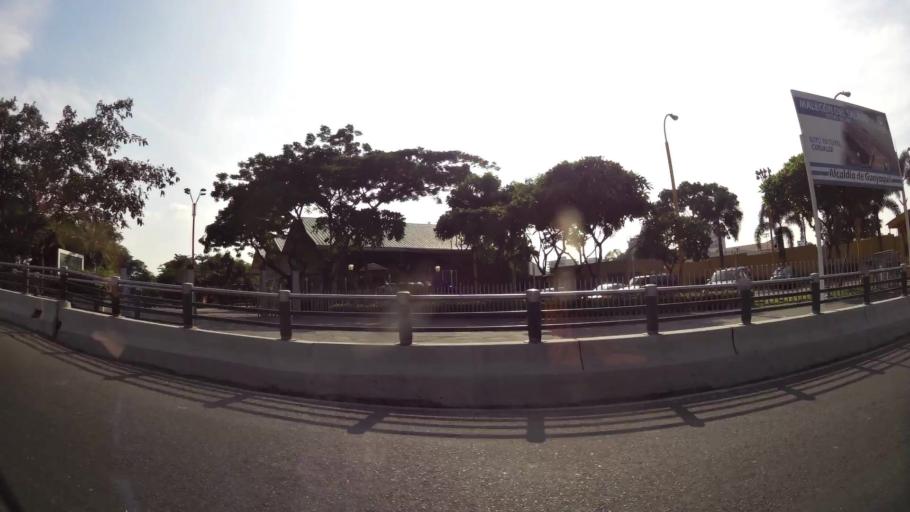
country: EC
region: Guayas
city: Guayaquil
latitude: -2.1894
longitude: -79.9006
